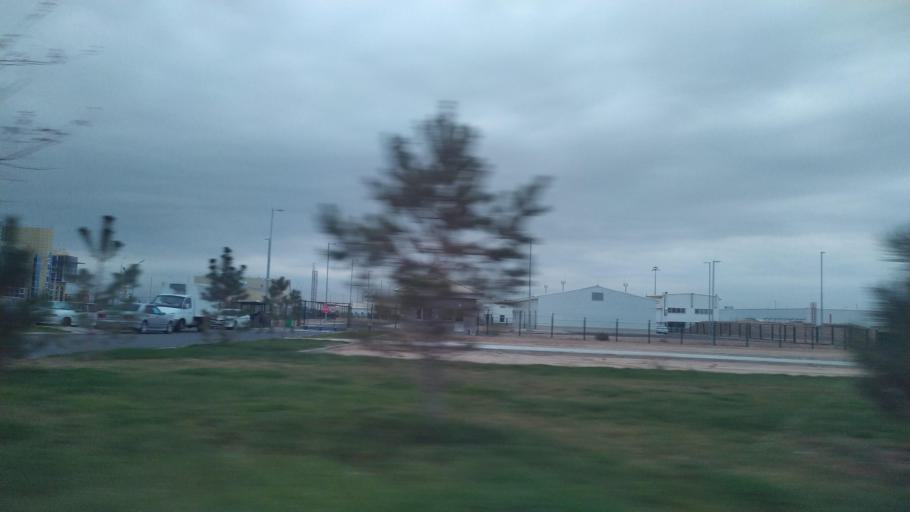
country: KZ
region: Ongtustik Qazaqstan
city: Kentau
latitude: 43.3159
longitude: 68.5456
